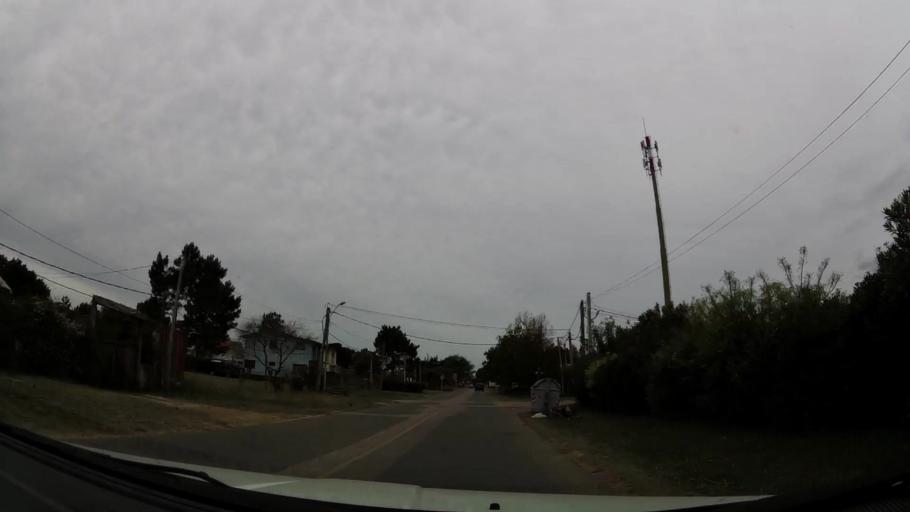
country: UY
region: Maldonado
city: Maldonado
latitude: -34.9002
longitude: -54.9954
